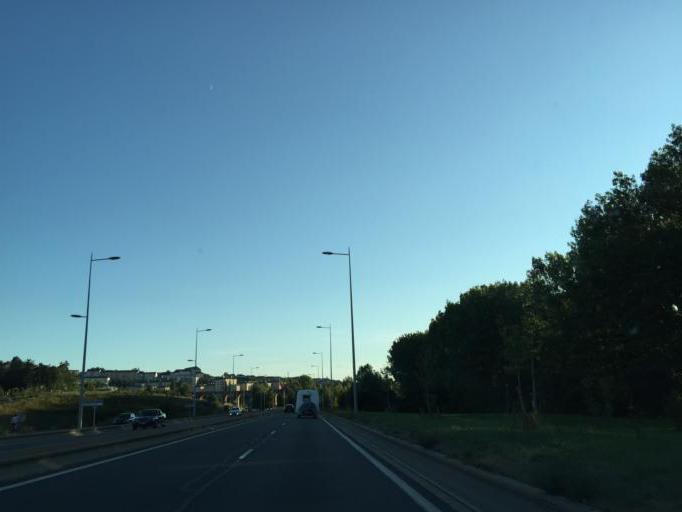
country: FR
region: Midi-Pyrenees
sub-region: Departement de l'Aveyron
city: Rodez
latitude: 44.3684
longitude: 2.5805
